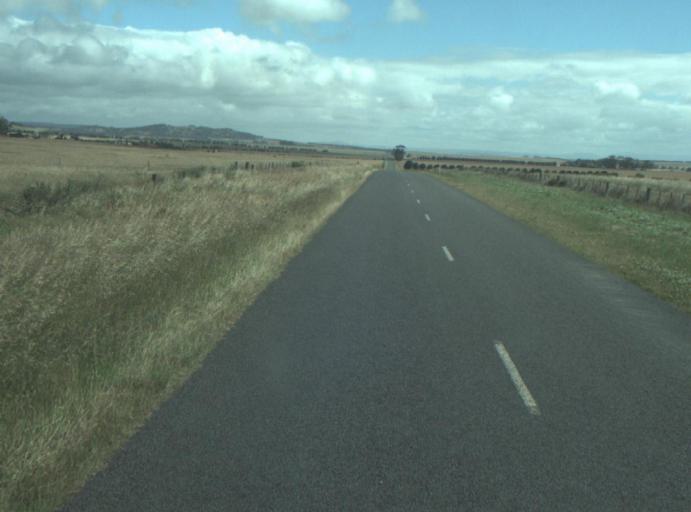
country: AU
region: Victoria
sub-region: Greater Geelong
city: Lara
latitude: -37.9392
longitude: 144.3100
